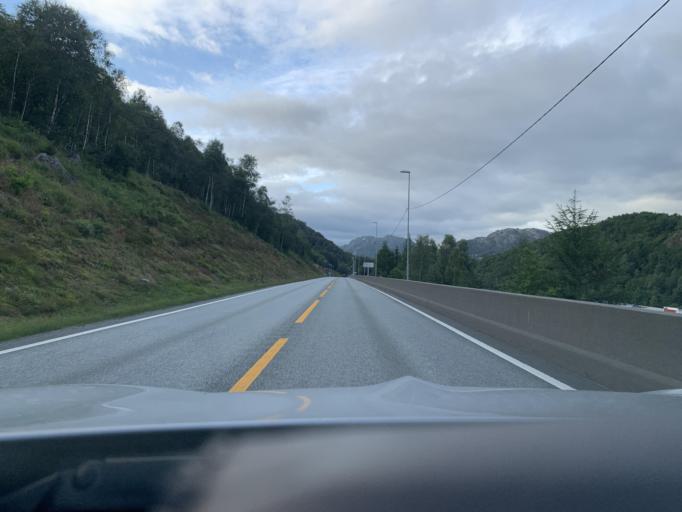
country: NO
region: Rogaland
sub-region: Bjerkreim
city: Vikesa
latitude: 58.5905
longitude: 6.0777
